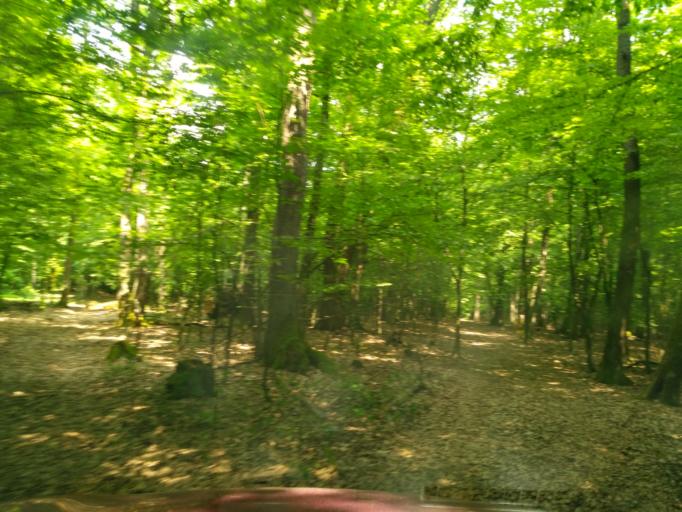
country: SK
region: Kosicky
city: Moldava nad Bodvou
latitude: 48.6552
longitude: 21.0342
